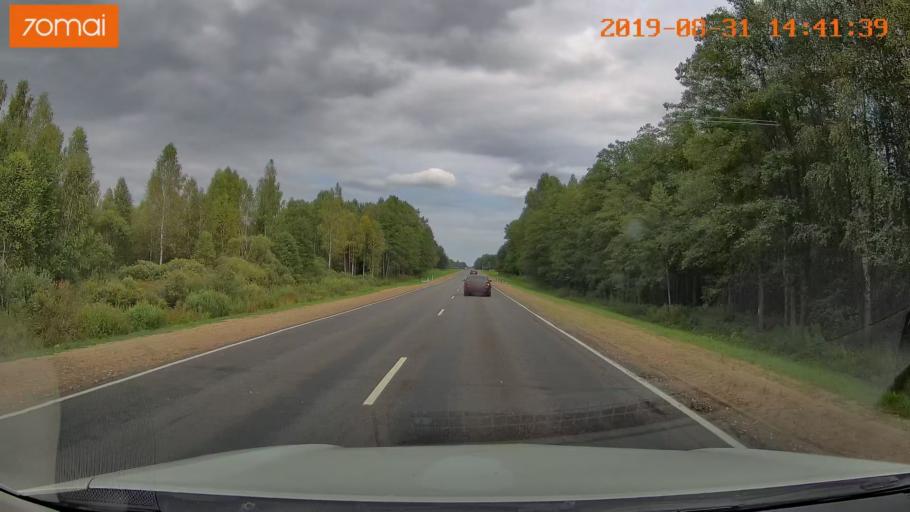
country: RU
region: Smolensk
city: Yekimovichi
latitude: 54.2039
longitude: 33.5940
